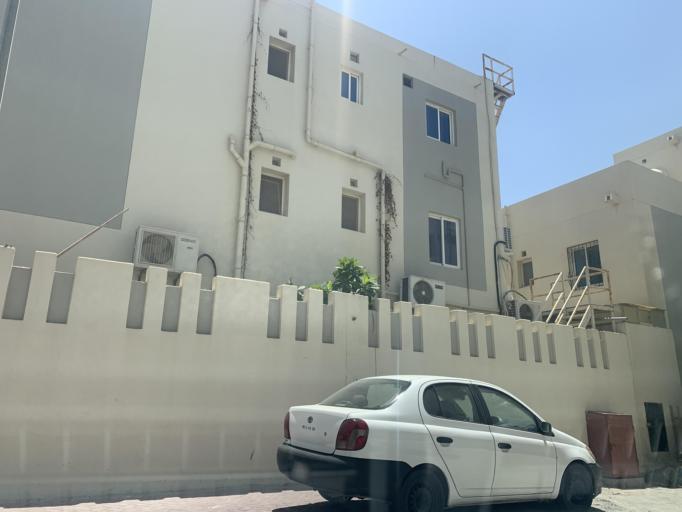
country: BH
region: Manama
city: Jidd Hafs
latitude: 26.2337
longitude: 50.4641
